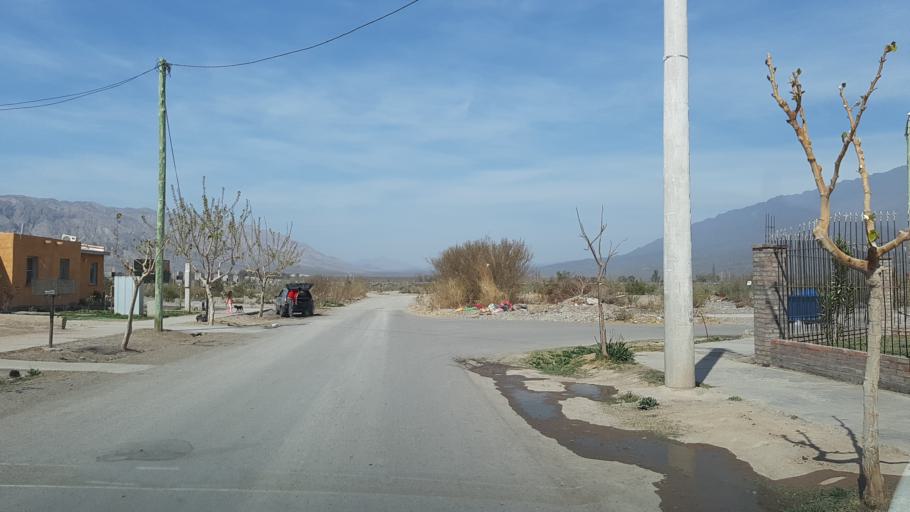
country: AR
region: San Juan
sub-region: Departamento de Zonda
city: Zonda
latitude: -31.5464
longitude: -68.7397
